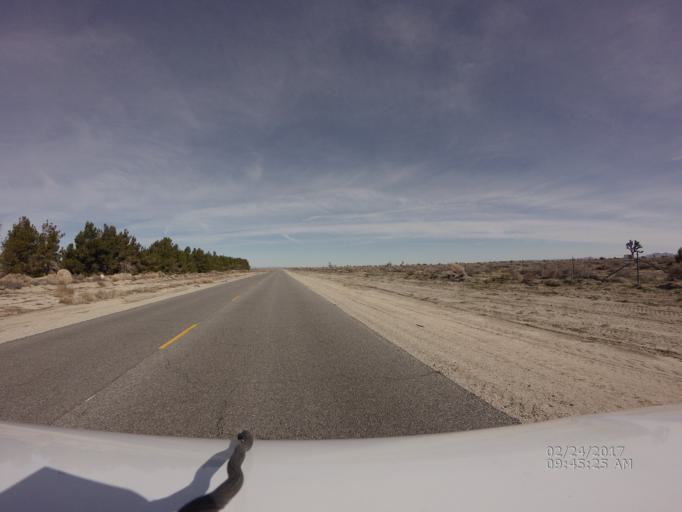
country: US
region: California
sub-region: Los Angeles County
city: Littlerock
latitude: 34.6052
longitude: -118.0051
